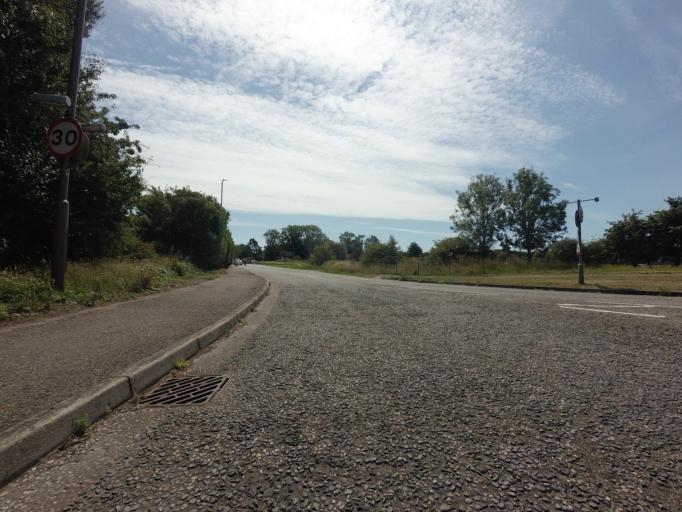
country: GB
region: England
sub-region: Kent
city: Stone
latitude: 50.9984
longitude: 0.8323
